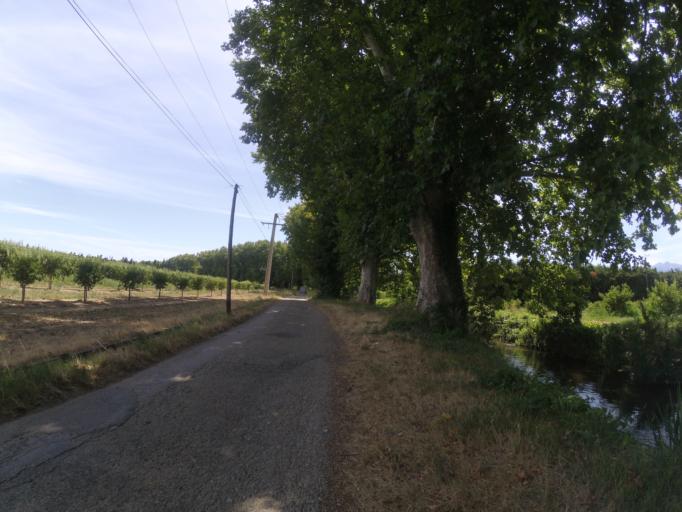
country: FR
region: Languedoc-Roussillon
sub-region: Departement des Pyrenees-Orientales
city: Ille-sur-Tet
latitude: 42.6735
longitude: 2.6521
